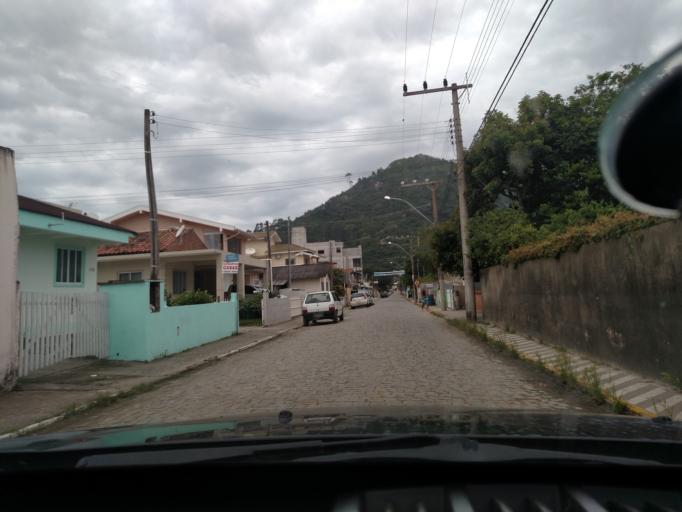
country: BR
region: Santa Catarina
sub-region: Porto Belo
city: Porto Belo
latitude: -27.1970
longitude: -48.5002
